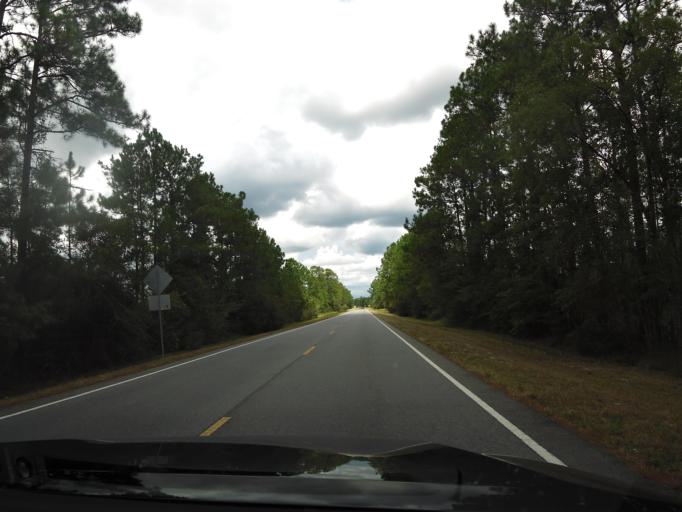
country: US
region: Georgia
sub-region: Brantley County
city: Nahunta
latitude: 31.1400
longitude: -81.9944
